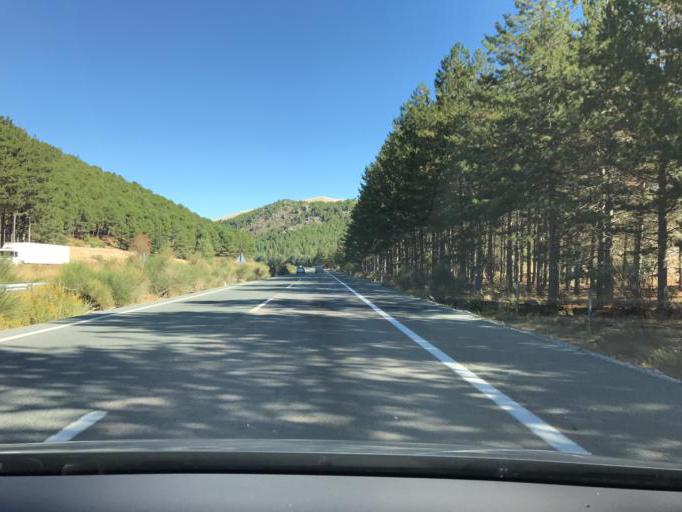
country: ES
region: Andalusia
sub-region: Provincia de Granada
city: Beas de Granada
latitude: 37.2723
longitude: -3.4625
